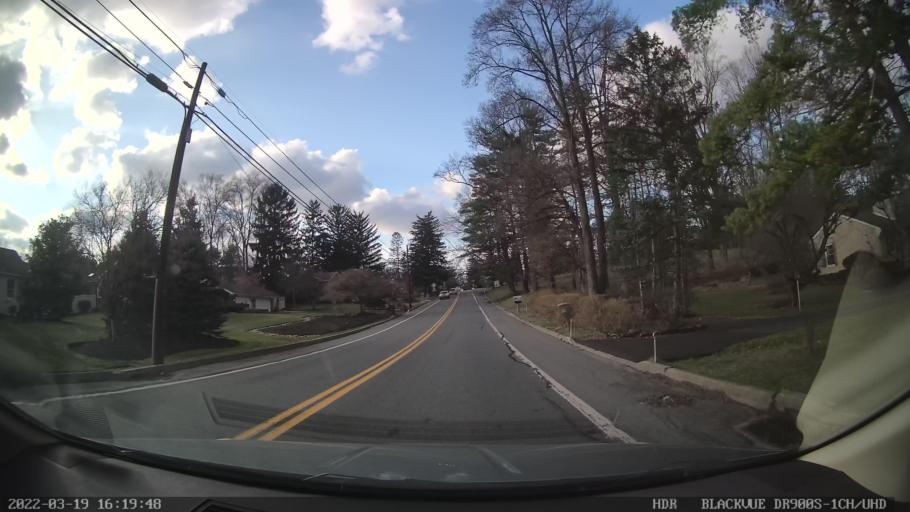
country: US
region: Pennsylvania
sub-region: Lehigh County
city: Dorneyville
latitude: 40.5741
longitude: -75.5002
